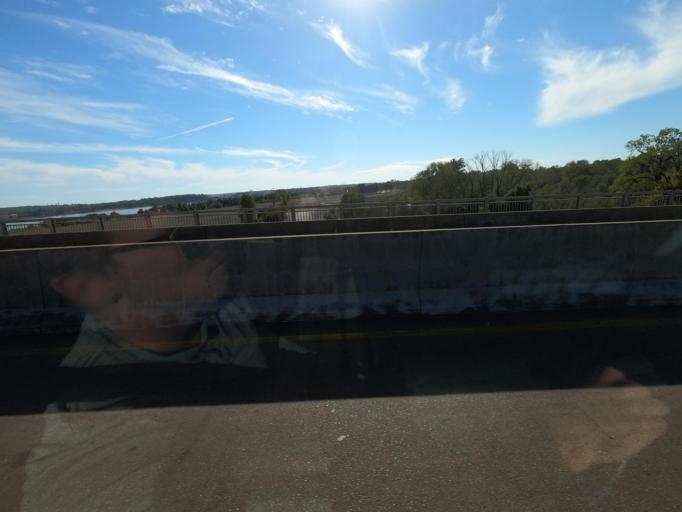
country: US
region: Tennessee
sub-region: Shelby County
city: Memphis
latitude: 35.1333
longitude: -90.0832
